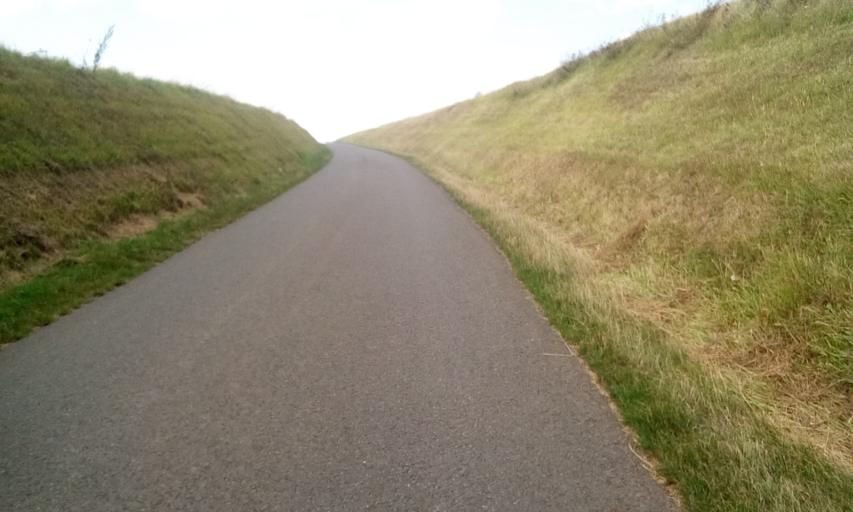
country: FR
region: Lower Normandy
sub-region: Departement du Calvados
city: Saint-Sylvain
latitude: 49.0730
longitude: -0.1994
